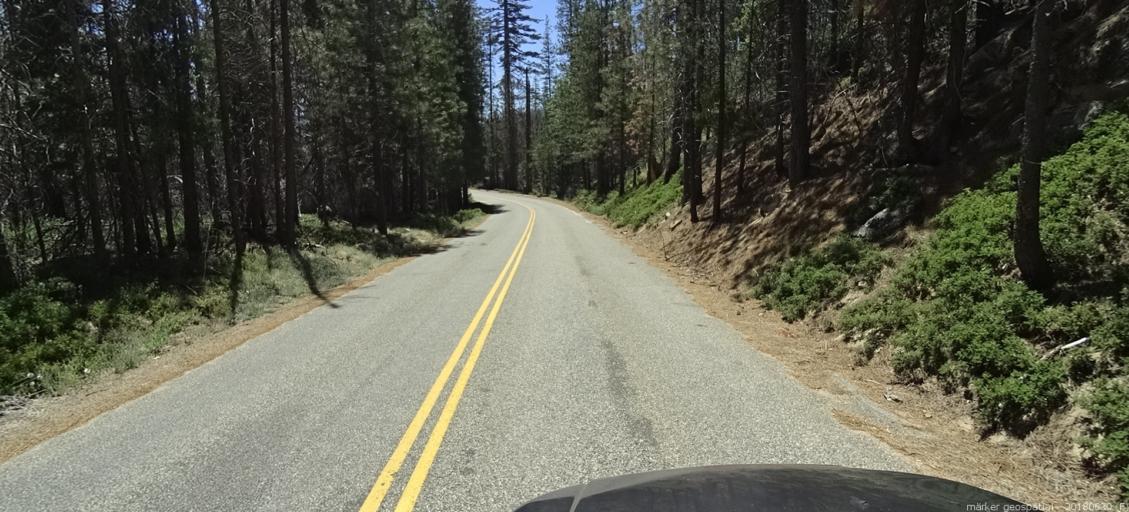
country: US
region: California
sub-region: Fresno County
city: Auberry
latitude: 37.3329
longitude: -119.3689
